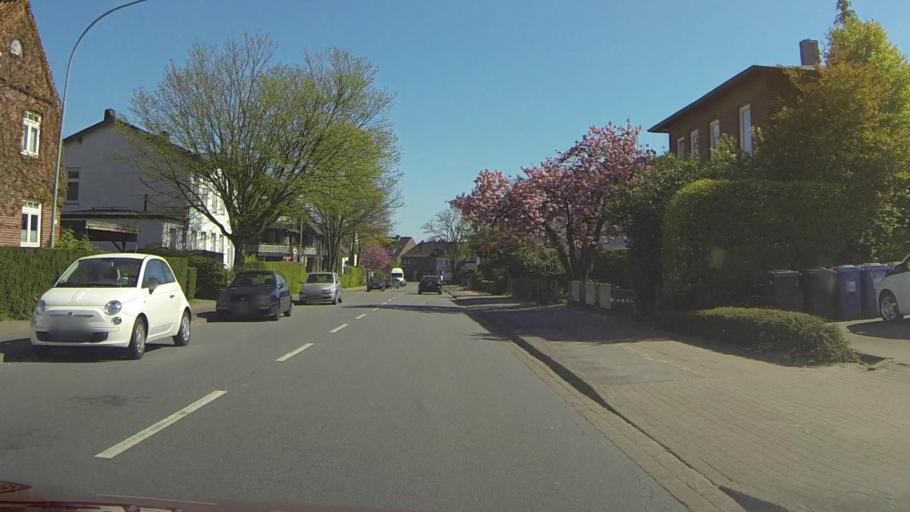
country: DE
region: Schleswig-Holstein
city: Pinneberg
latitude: 53.6662
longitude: 9.7881
